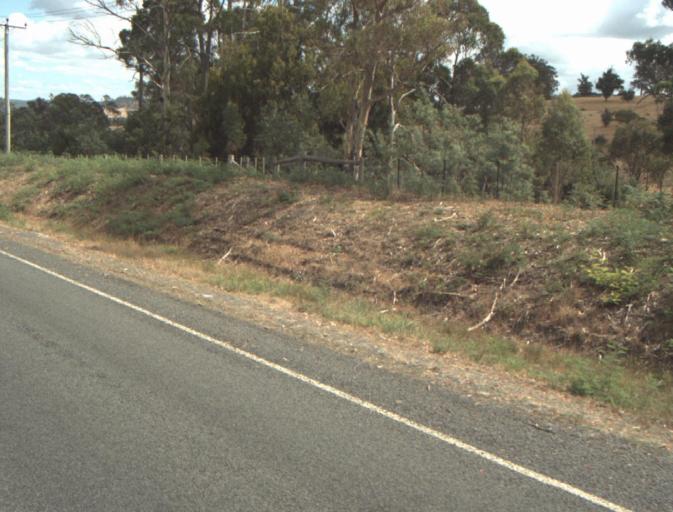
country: AU
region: Tasmania
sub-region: Launceston
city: Mayfield
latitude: -41.3047
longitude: 147.0487
